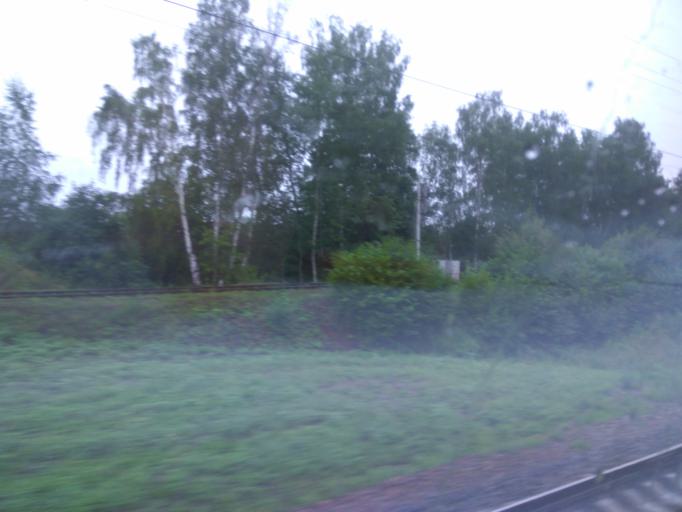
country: RU
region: Moskovskaya
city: Stupino
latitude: 54.9166
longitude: 38.0717
